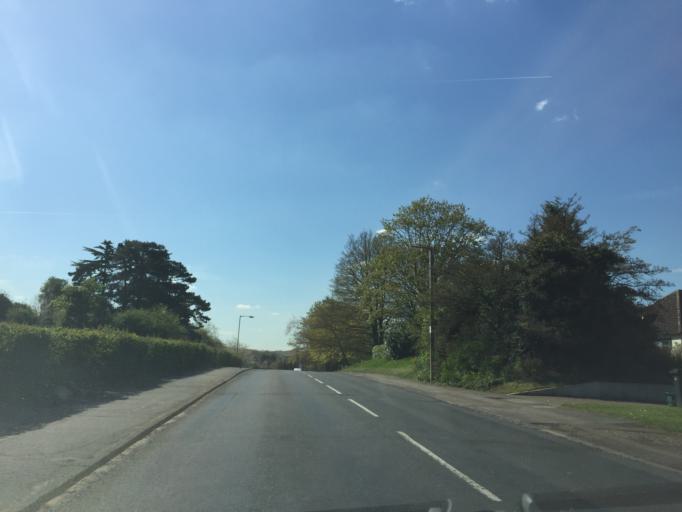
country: GB
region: England
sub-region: Essex
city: Harlow
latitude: 51.7651
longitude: 0.0844
